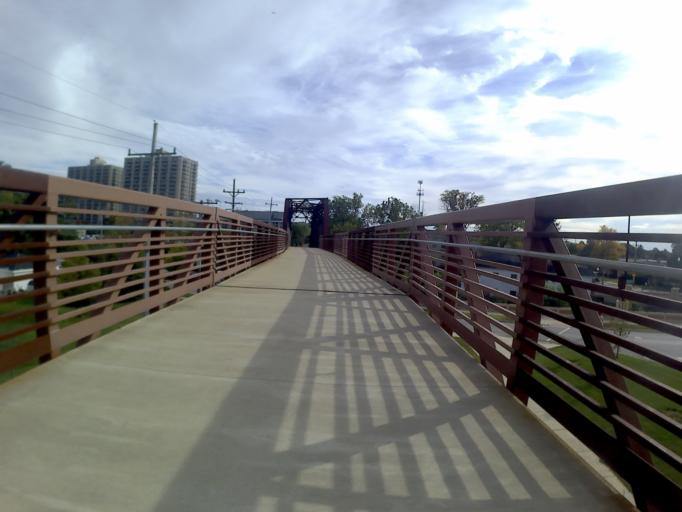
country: US
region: Illinois
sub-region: DuPage County
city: Wheaton
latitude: 41.8660
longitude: -88.1168
